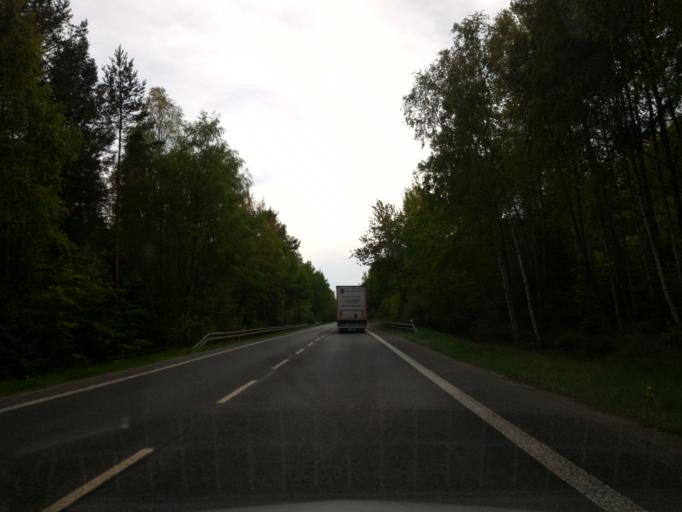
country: CZ
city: Novy Bor
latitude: 50.7840
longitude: 14.5889
